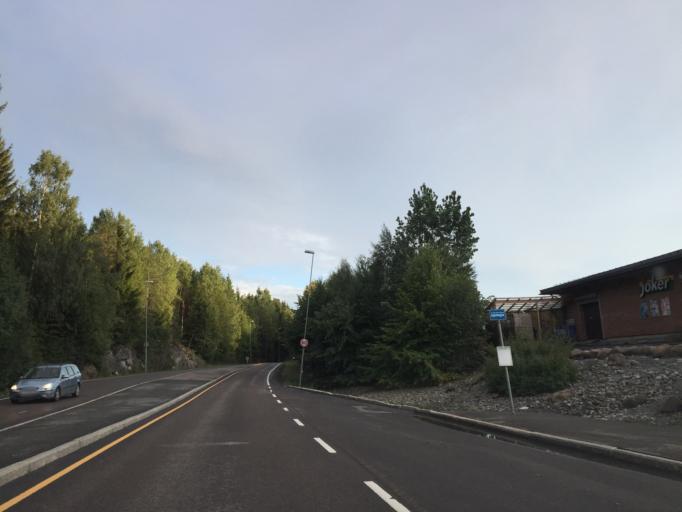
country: NO
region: Akershus
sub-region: Ski
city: Ski
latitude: 59.7720
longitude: 10.8500
